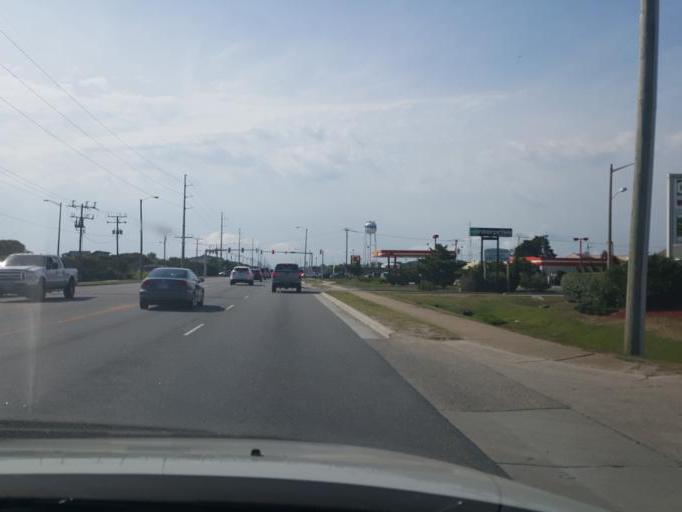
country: US
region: North Carolina
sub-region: Dare County
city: Kill Devil Hills
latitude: 36.0353
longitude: -75.6739
